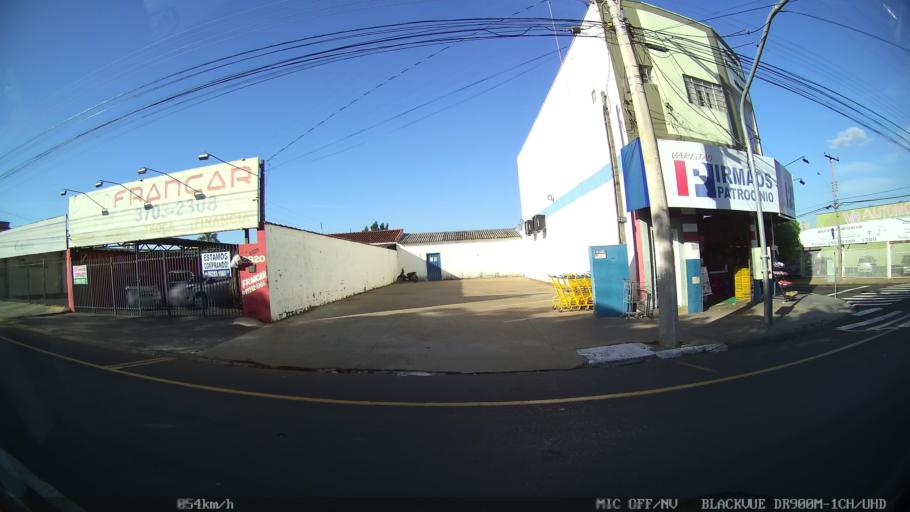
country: BR
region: Sao Paulo
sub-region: Franca
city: Franca
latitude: -20.5133
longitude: -47.3987
